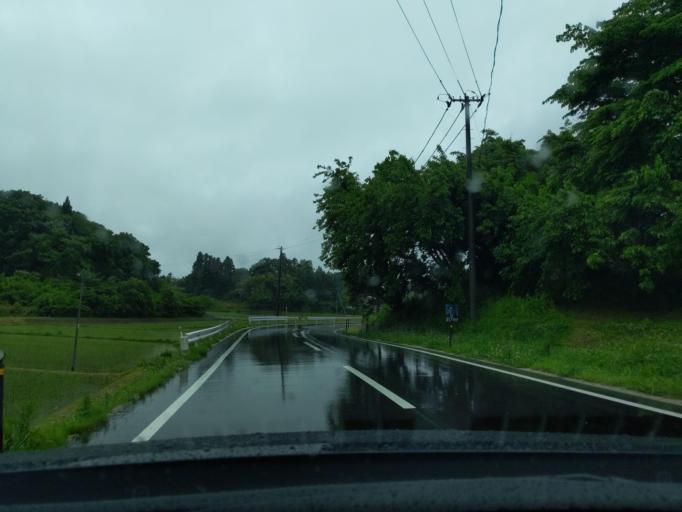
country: JP
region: Fukushima
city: Nihommatsu
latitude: 37.5216
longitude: 140.4811
